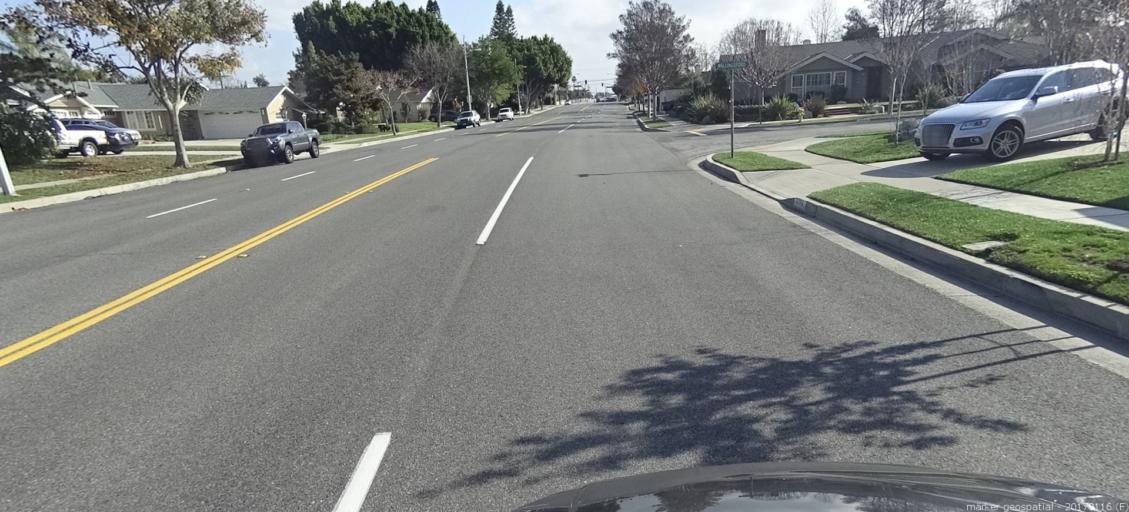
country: US
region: California
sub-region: Orange County
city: Los Alamitos
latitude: 33.7958
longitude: -118.0749
